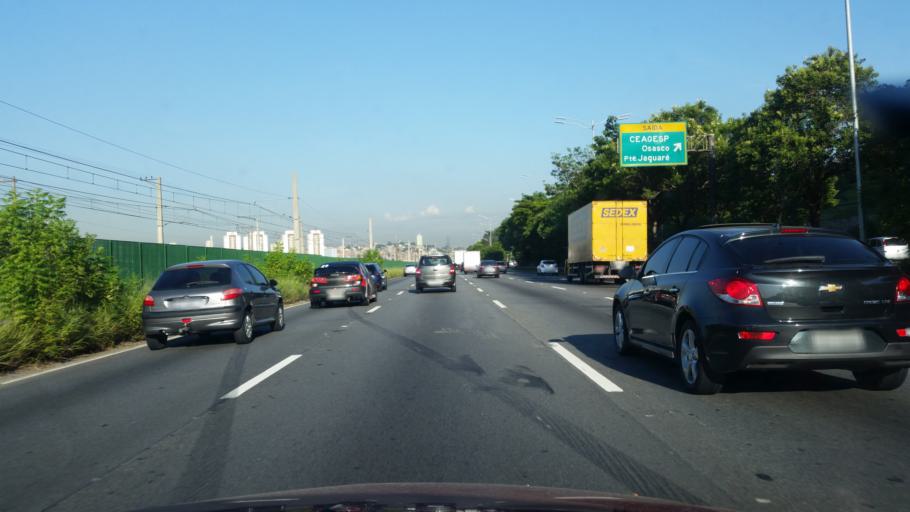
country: BR
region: Sao Paulo
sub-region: Osasco
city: Osasco
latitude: -23.5521
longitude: -46.7226
